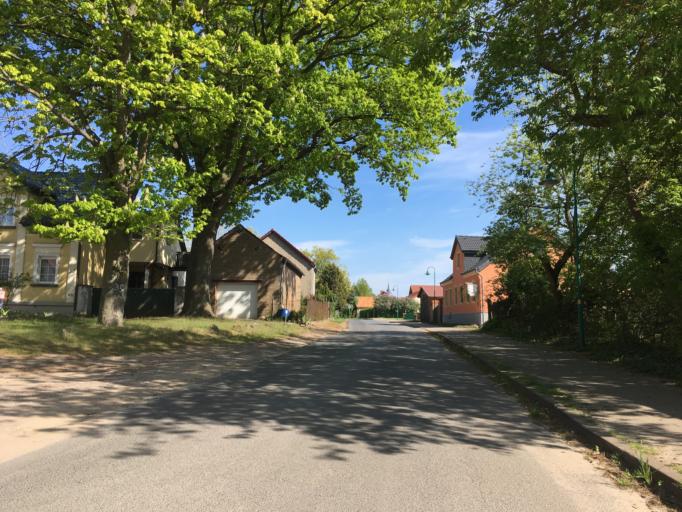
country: DE
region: Brandenburg
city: Rudnitz
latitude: 52.7229
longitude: 13.6189
